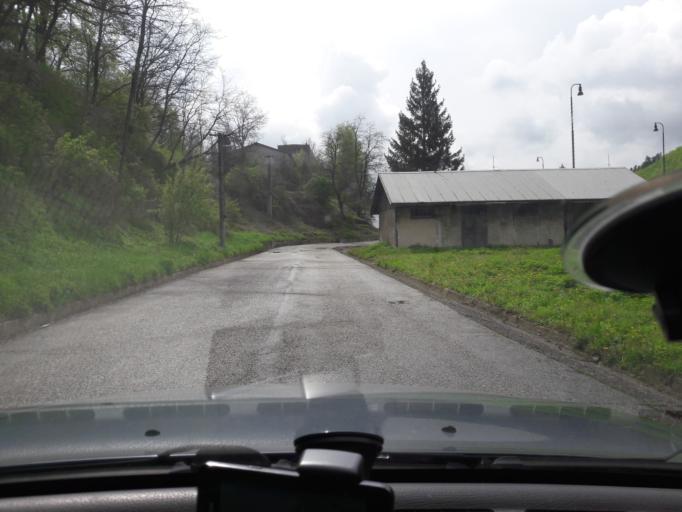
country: SK
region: Banskobystricky
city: Tisovec
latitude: 48.6897
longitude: 19.9375
